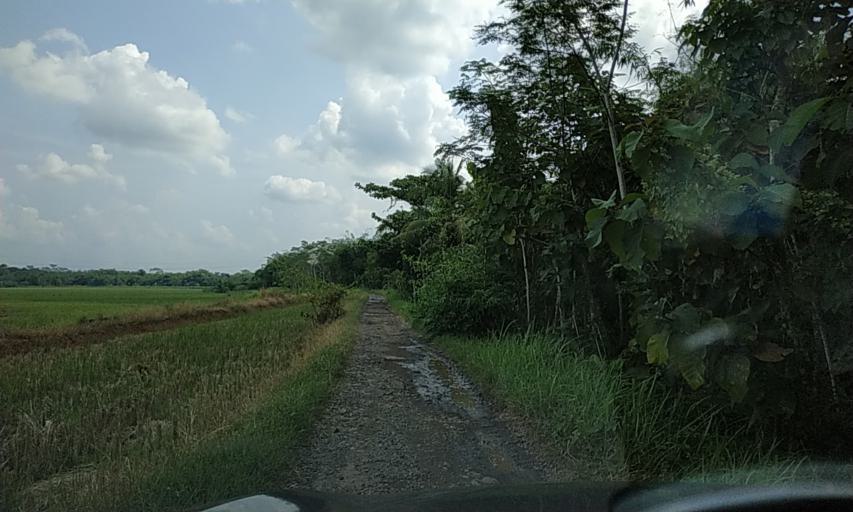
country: ID
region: Central Java
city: Sogati
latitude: -7.3349
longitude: 108.6715
